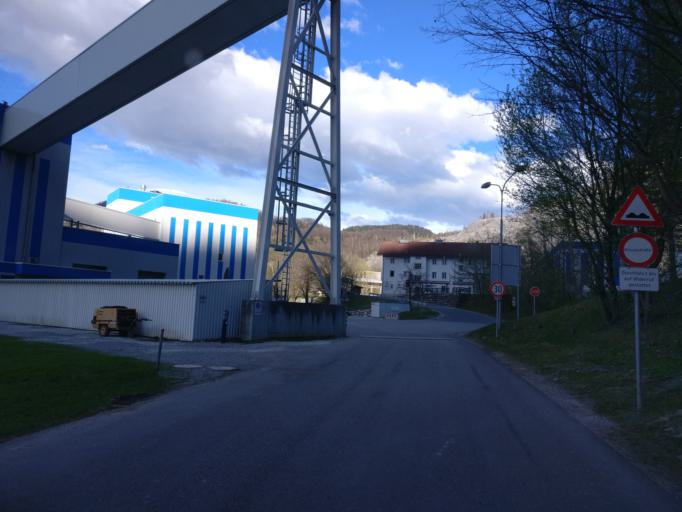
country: AT
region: Salzburg
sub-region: Politischer Bezirk Hallein
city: Golling an der Salzach
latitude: 47.5776
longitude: 13.1770
